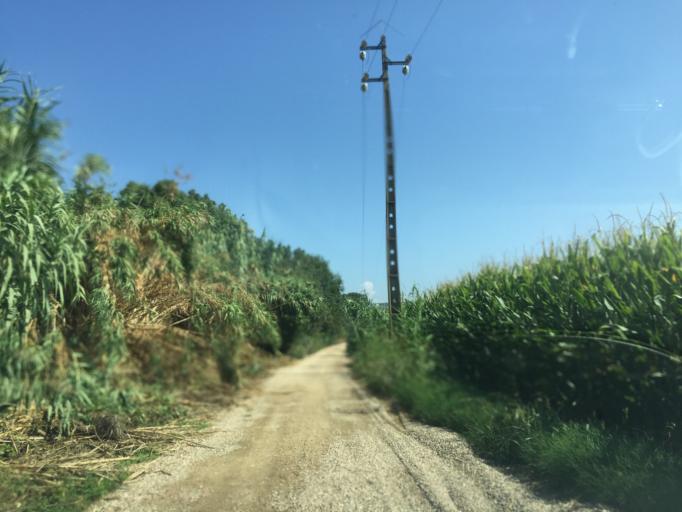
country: PT
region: Santarem
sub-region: Chamusca
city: Vila Nova da Barquinha
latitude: 39.4510
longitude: -8.4482
